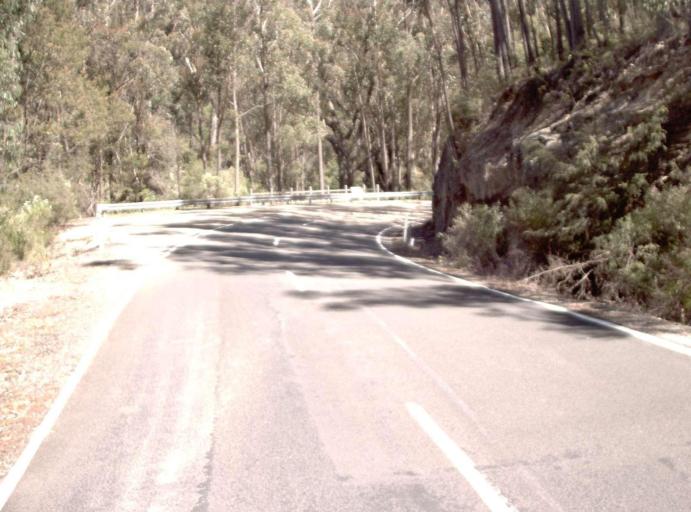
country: AU
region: Victoria
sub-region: East Gippsland
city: Lakes Entrance
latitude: -37.3699
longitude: 148.2196
